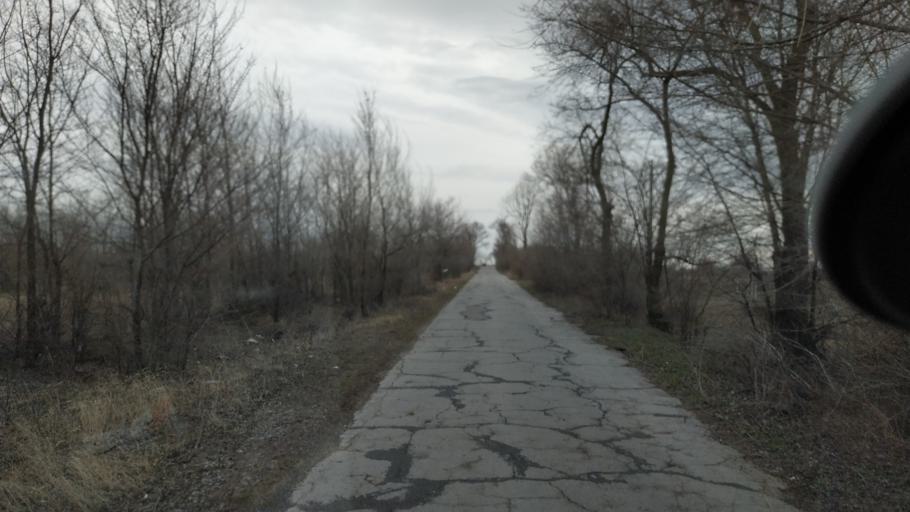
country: MD
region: Telenesti
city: Cocieri
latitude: 47.3262
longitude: 29.0951
